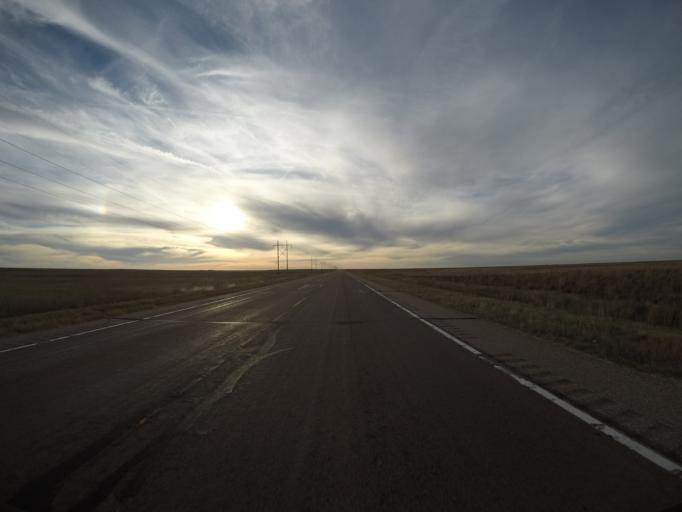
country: US
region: Colorado
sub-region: Yuma County
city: Yuma
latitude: 39.6553
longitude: -102.7758
